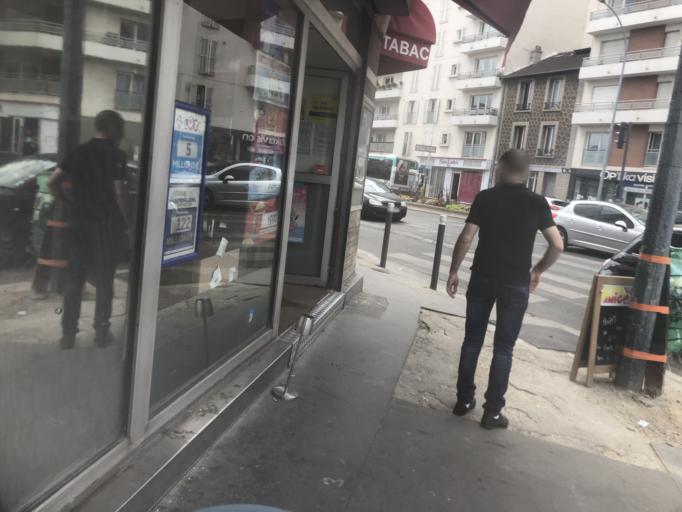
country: FR
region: Ile-de-France
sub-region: Paris
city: Saint-Ouen
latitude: 48.9152
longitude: 2.3380
